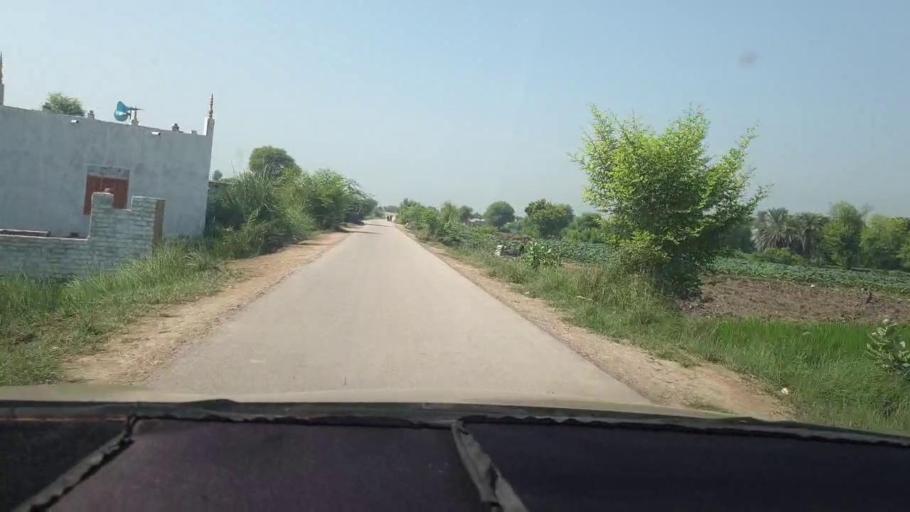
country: PK
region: Sindh
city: Kambar
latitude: 27.5813
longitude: 68.0466
